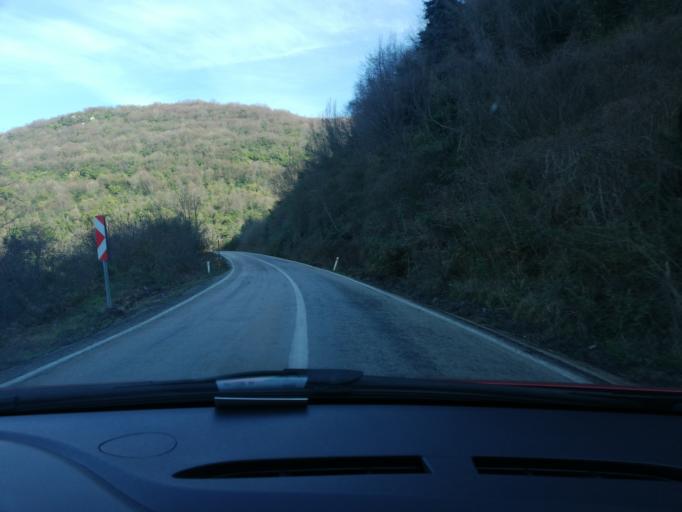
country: TR
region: Bartin
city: Kurucasile
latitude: 41.8444
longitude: 32.7662
